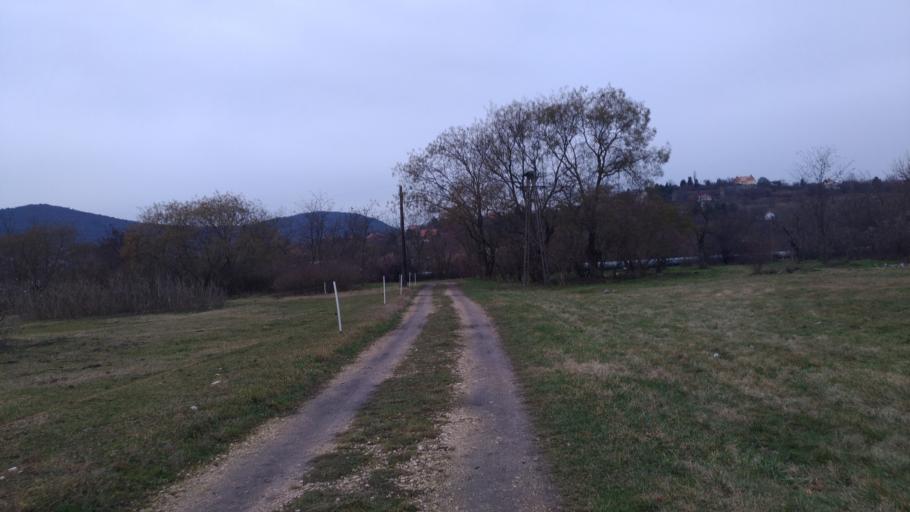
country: HU
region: Pest
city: Urom
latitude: 47.5731
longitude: 19.0345
